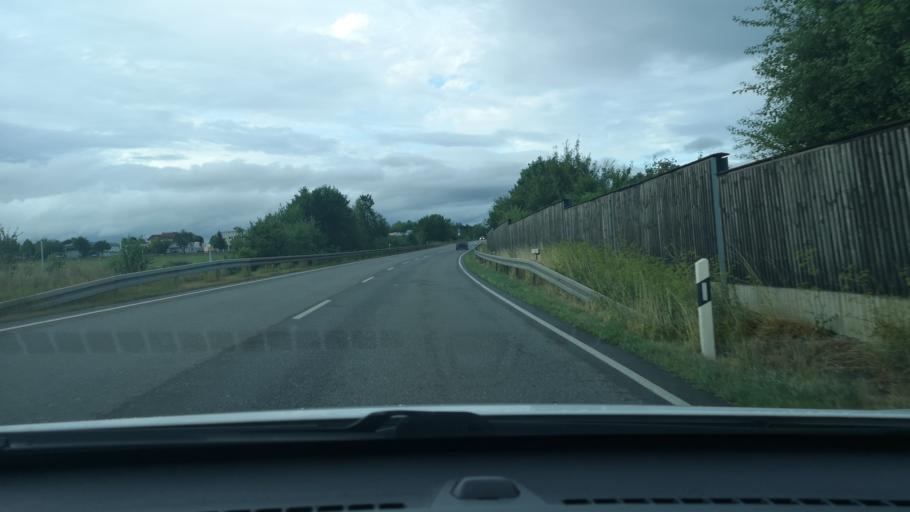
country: DE
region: Baden-Wuerttemberg
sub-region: Freiburg Region
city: Zimmern ob Rottweil
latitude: 48.1609
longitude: 8.6029
